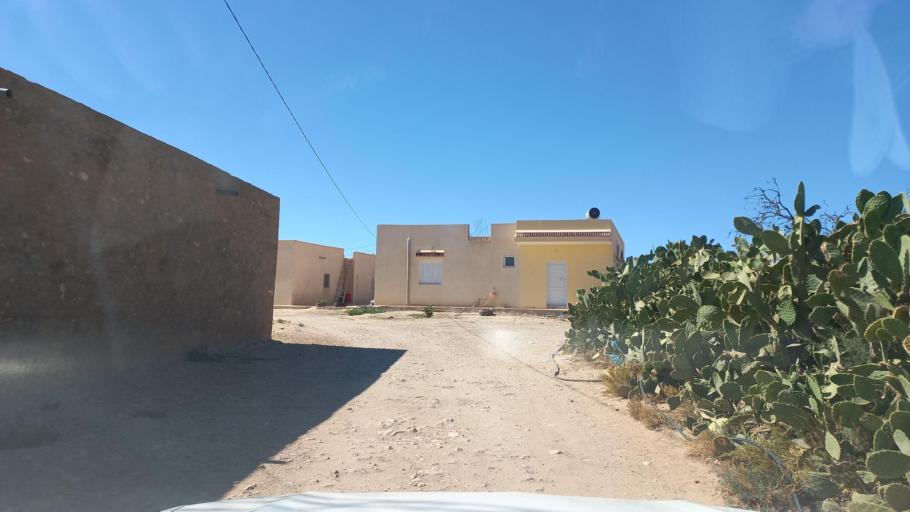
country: TN
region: Al Qasrayn
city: Sbiba
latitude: 35.3789
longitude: 9.0734
